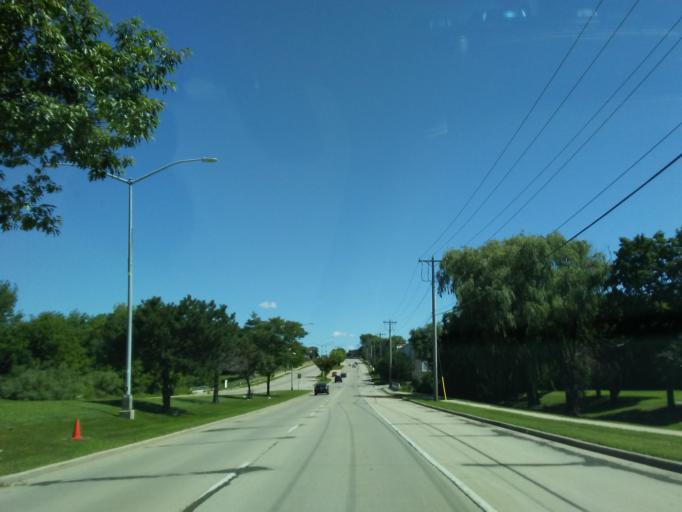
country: US
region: Wisconsin
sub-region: Dane County
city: Madison
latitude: 43.0220
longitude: -89.4167
